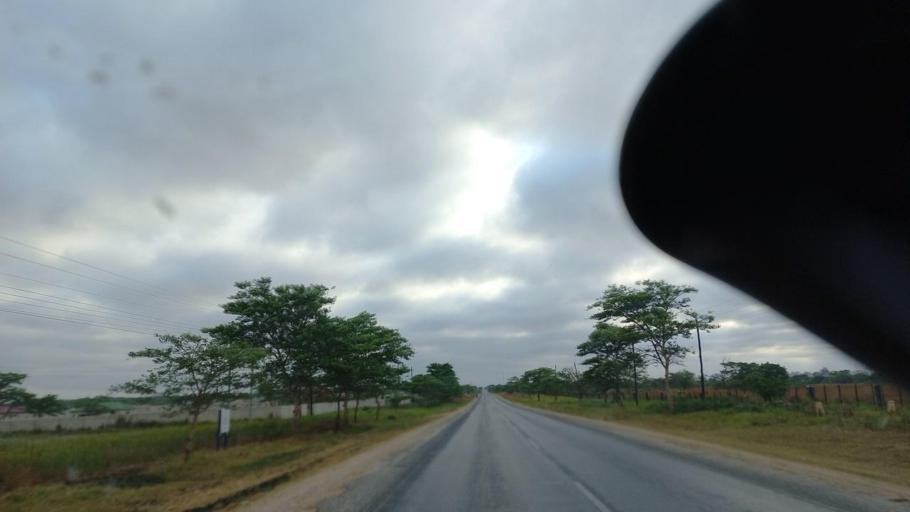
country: ZM
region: Lusaka
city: Chongwe
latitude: -15.3523
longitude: 28.4906
